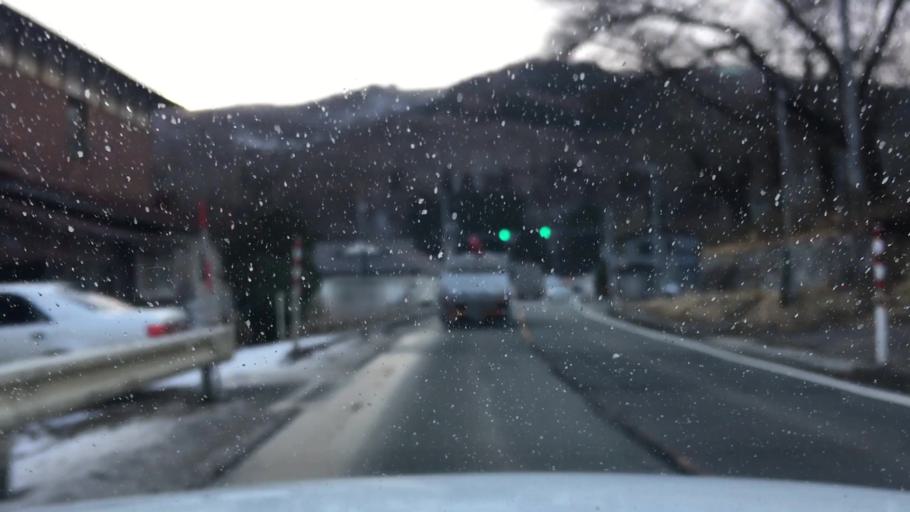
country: JP
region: Iwate
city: Morioka-shi
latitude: 39.6723
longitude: 141.1985
